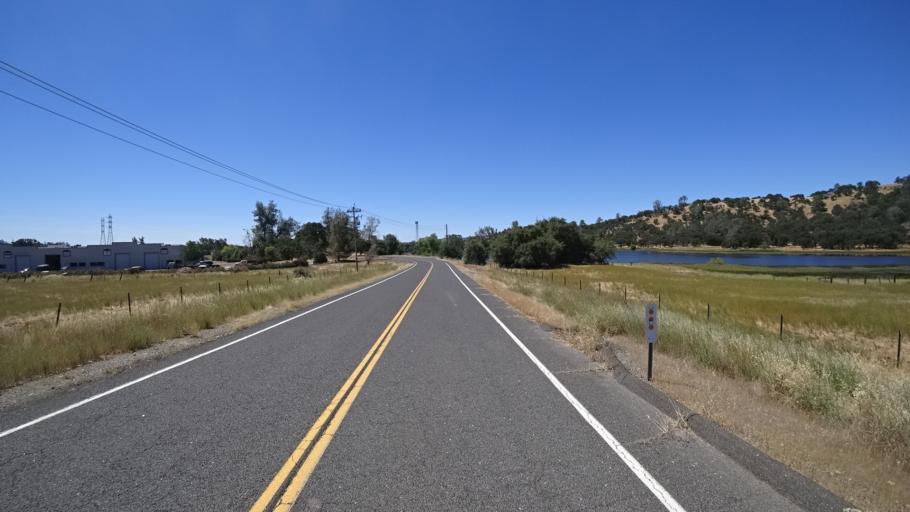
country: US
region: California
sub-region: Calaveras County
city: Copperopolis
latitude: 37.9858
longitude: -120.6483
